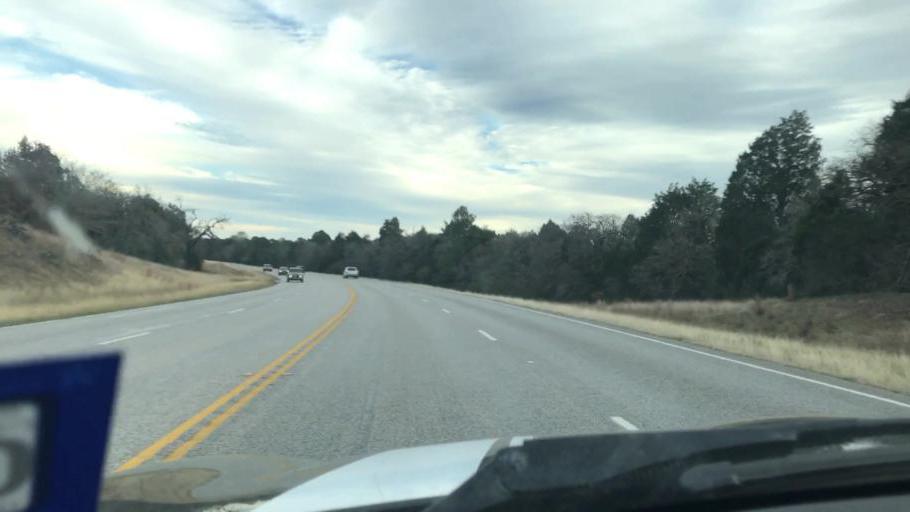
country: US
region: Texas
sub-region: Bastrop County
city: Camp Swift
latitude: 30.2476
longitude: -97.2227
